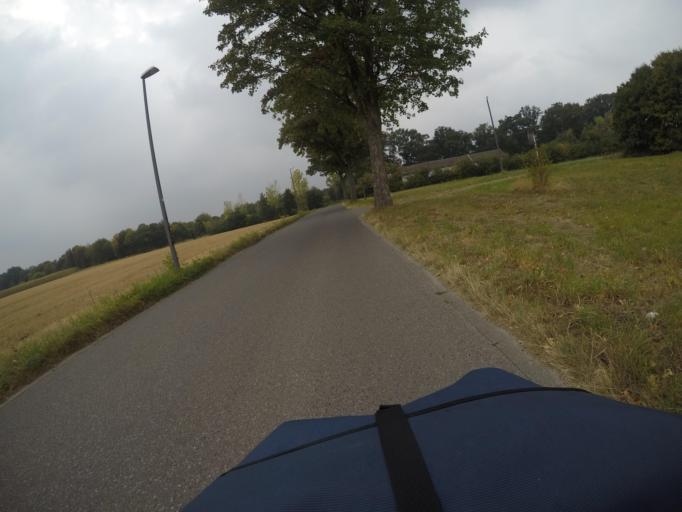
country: DE
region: North Rhine-Westphalia
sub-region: Regierungsbezirk Dusseldorf
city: Krefeld
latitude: 51.2990
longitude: 6.6064
